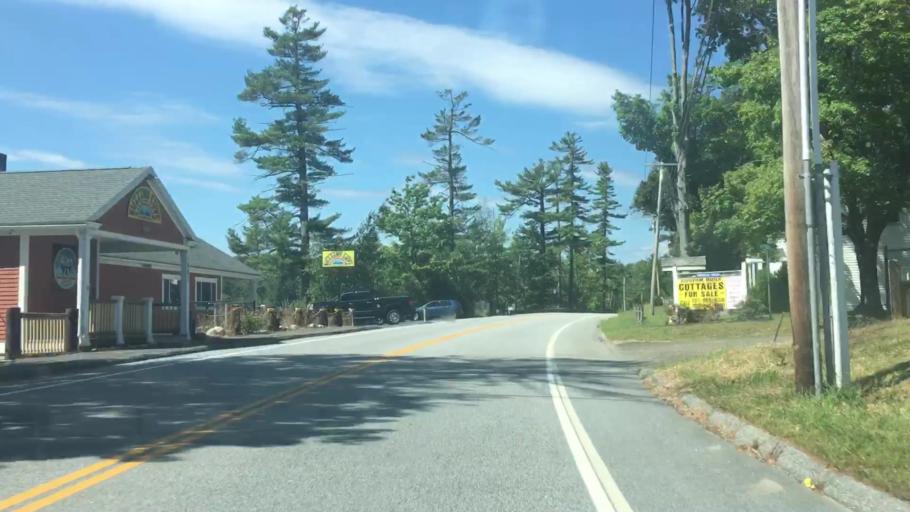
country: US
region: Maine
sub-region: Kennebec County
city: Monmouth
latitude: 44.1871
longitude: -69.9628
